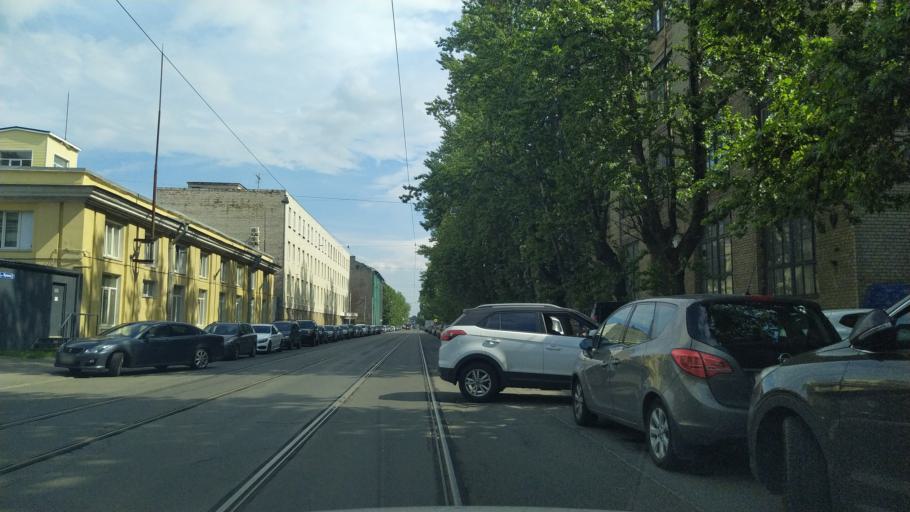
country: RU
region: Leningrad
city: Finlyandskiy
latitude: 59.9667
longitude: 30.3874
